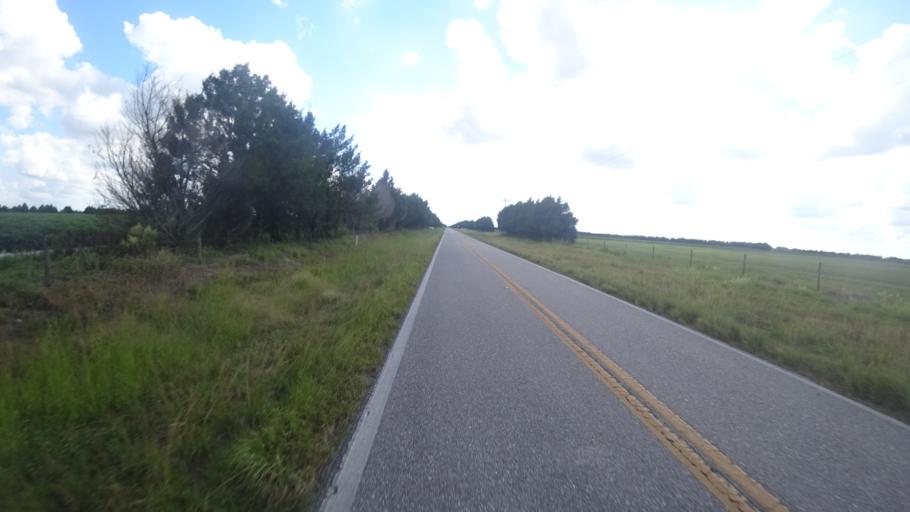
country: US
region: Florida
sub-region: DeSoto County
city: Arcadia
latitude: 27.3029
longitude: -82.1133
